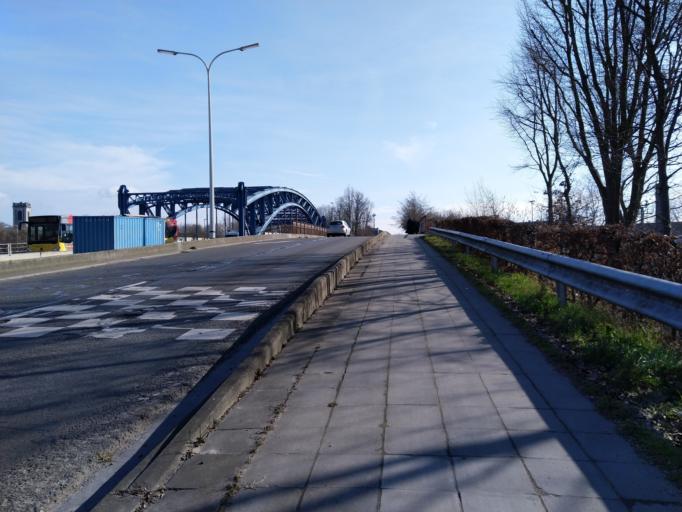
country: BE
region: Wallonia
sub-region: Province du Hainaut
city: Mons
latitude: 50.4505
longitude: 3.9366
